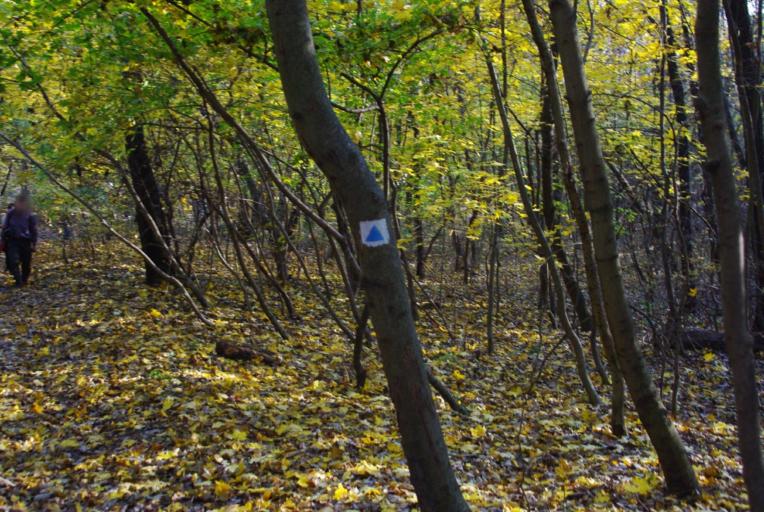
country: HU
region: Pest
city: Piliscsaba
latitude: 47.6443
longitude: 18.8351
